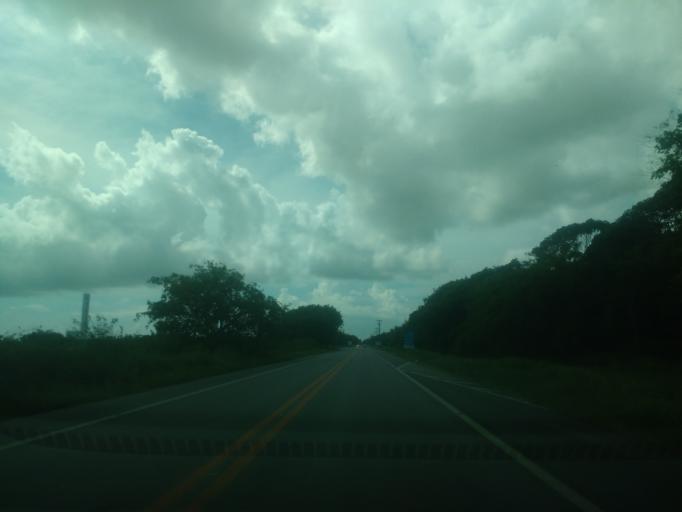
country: BR
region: Alagoas
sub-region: Marechal Deodoro
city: Marechal Deodoro
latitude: -9.6682
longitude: -35.8435
